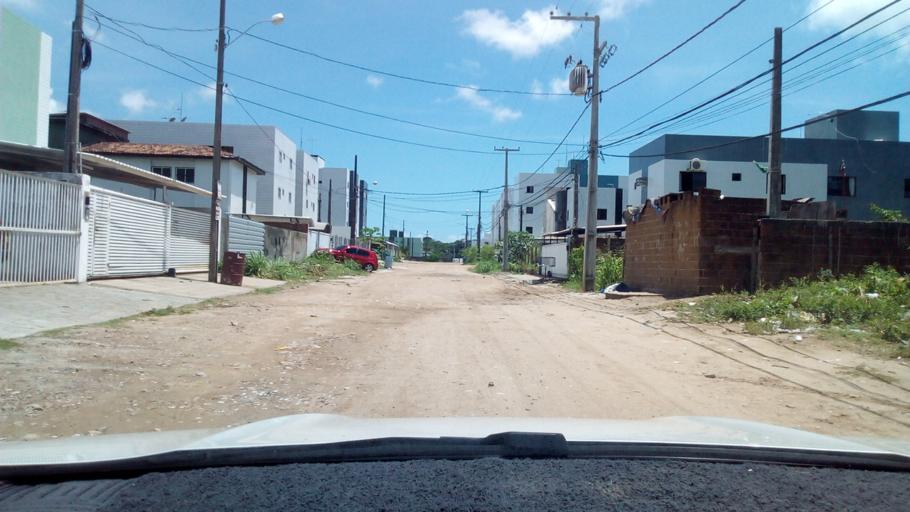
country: BR
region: Paraiba
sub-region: Joao Pessoa
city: Joao Pessoa
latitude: -7.1558
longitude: -34.8542
